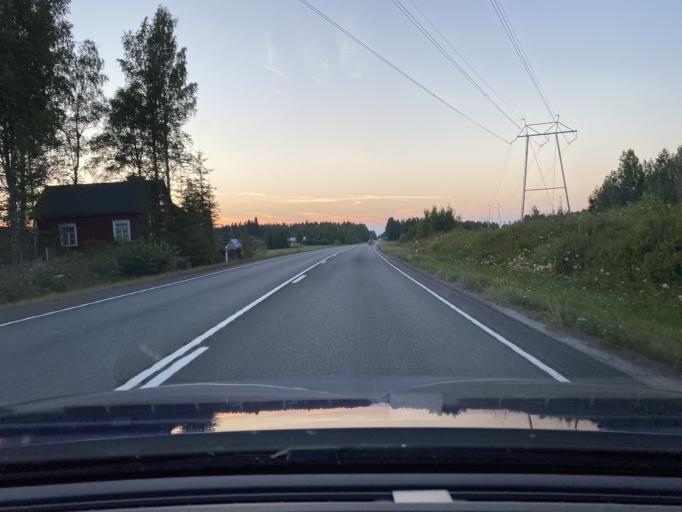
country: FI
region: Pirkanmaa
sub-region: Luoteis-Pirkanmaa
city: Ikaalinen
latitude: 61.8209
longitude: 22.9497
